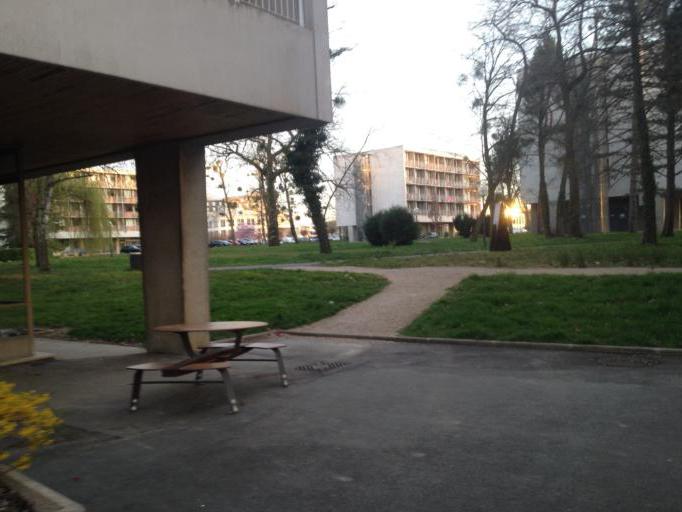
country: FR
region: Ile-de-France
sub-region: Departement des Yvelines
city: Jouy-en-Josas
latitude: 48.7581
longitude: 2.1670
